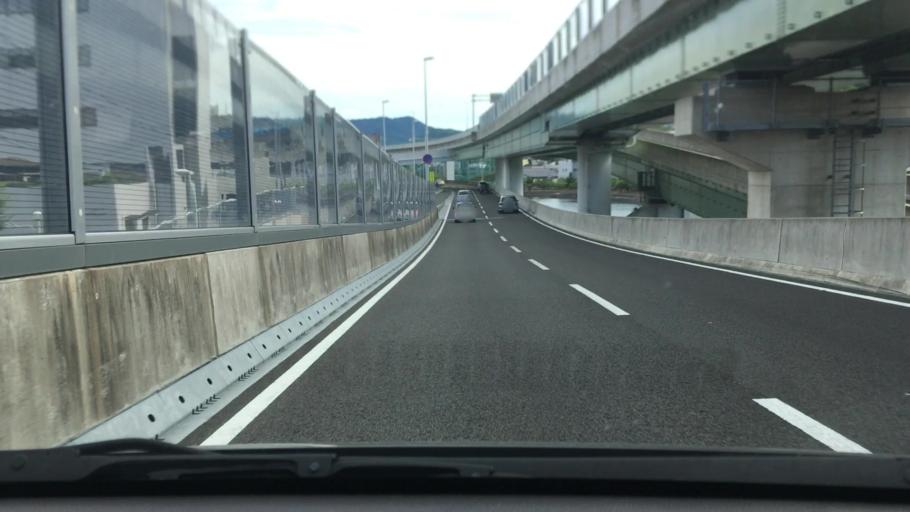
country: JP
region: Nagasaki
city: Nagasaki-shi
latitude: 32.7630
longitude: 129.8620
